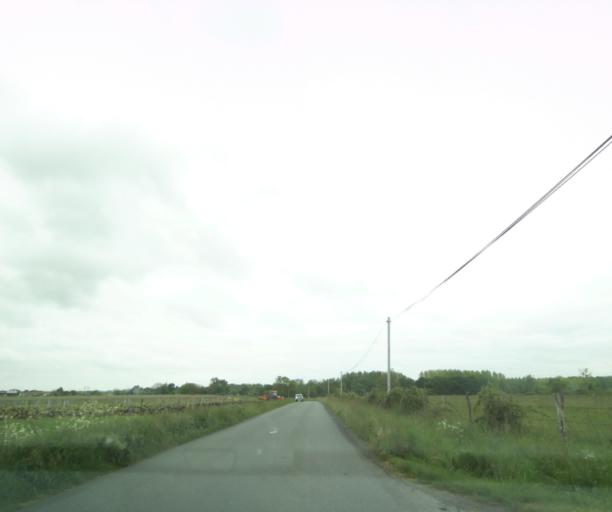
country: FR
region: Poitou-Charentes
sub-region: Departement de la Charente-Maritime
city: Chaniers
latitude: 45.7059
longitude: -0.5650
